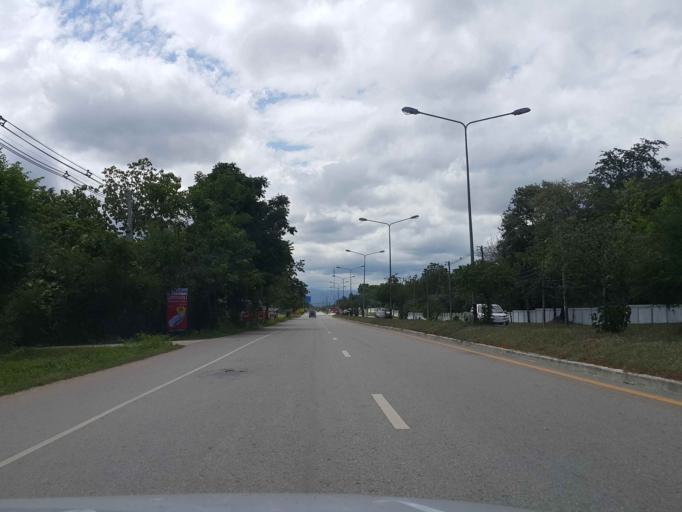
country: TH
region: Tak
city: Tak
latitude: 16.8793
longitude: 99.1421
